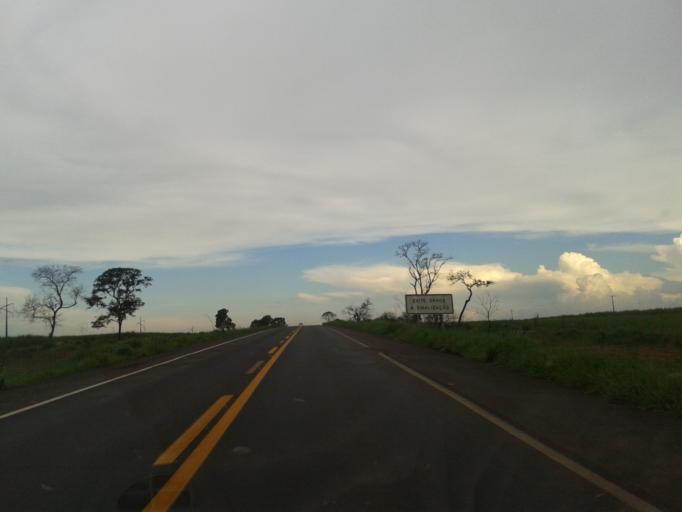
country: BR
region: Minas Gerais
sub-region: Santa Vitoria
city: Santa Vitoria
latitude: -18.8954
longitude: -50.1762
